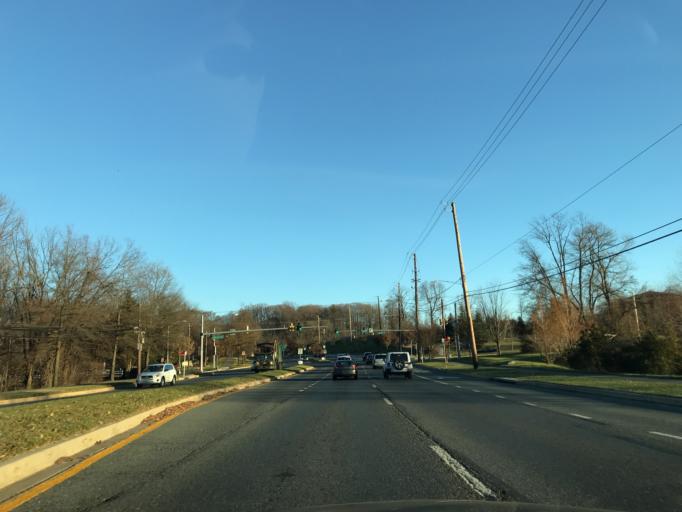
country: US
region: Maryland
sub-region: Montgomery County
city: Olney
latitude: 39.1454
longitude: -77.0486
